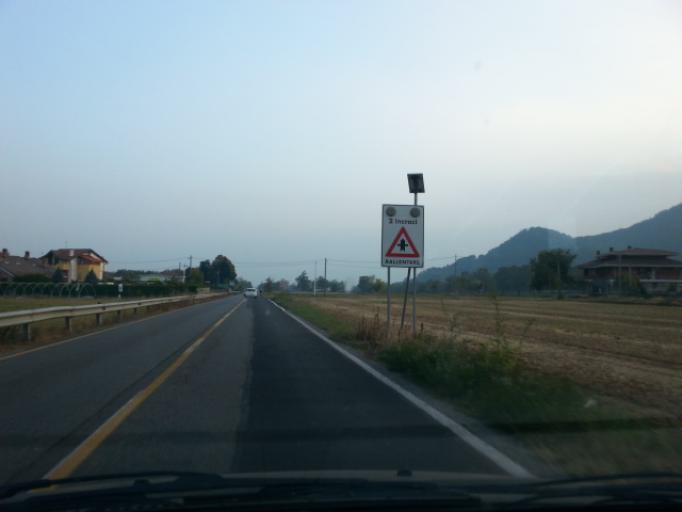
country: IT
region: Piedmont
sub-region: Provincia di Torino
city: Bruino
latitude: 45.0093
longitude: 7.4661
